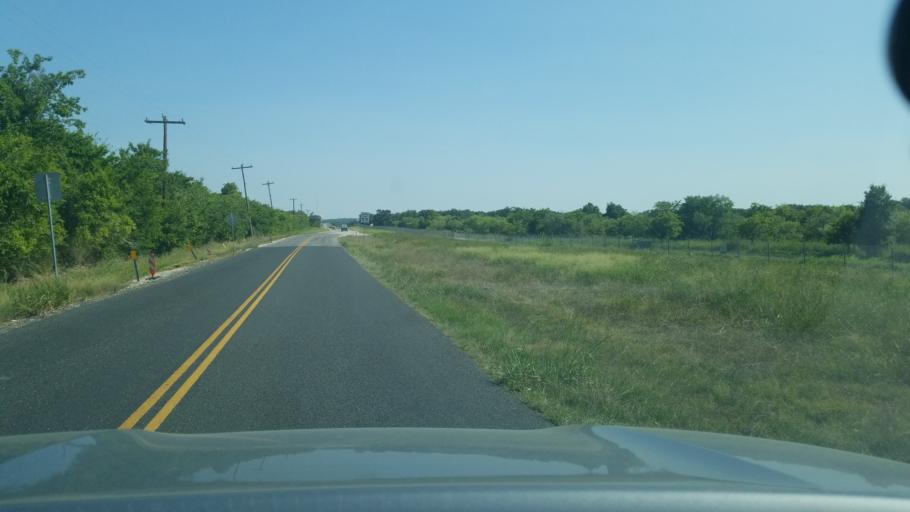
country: US
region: Texas
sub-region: Bexar County
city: Timberwood Park
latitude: 29.7384
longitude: -98.5129
